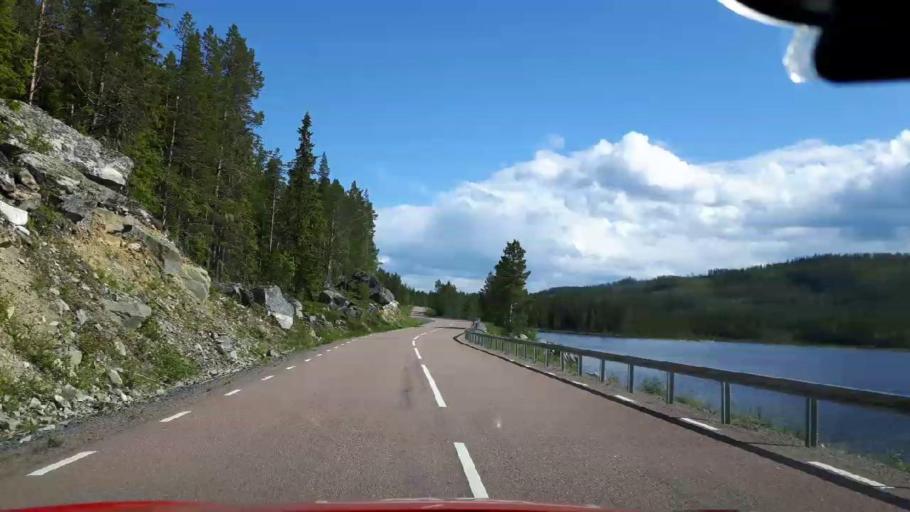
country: SE
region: Jaemtland
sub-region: Krokoms Kommun
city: Valla
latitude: 64.0252
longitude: 14.1991
